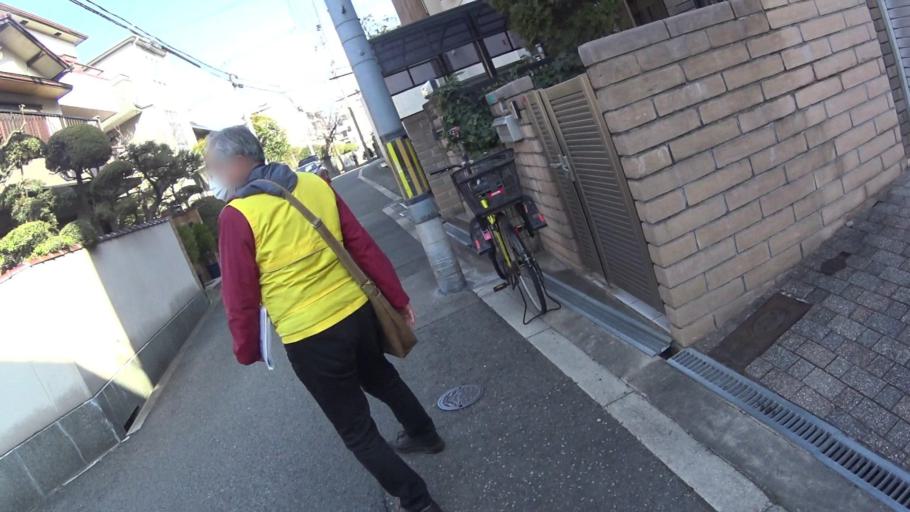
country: JP
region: Osaka
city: Sakai
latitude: 34.6257
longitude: 135.4971
